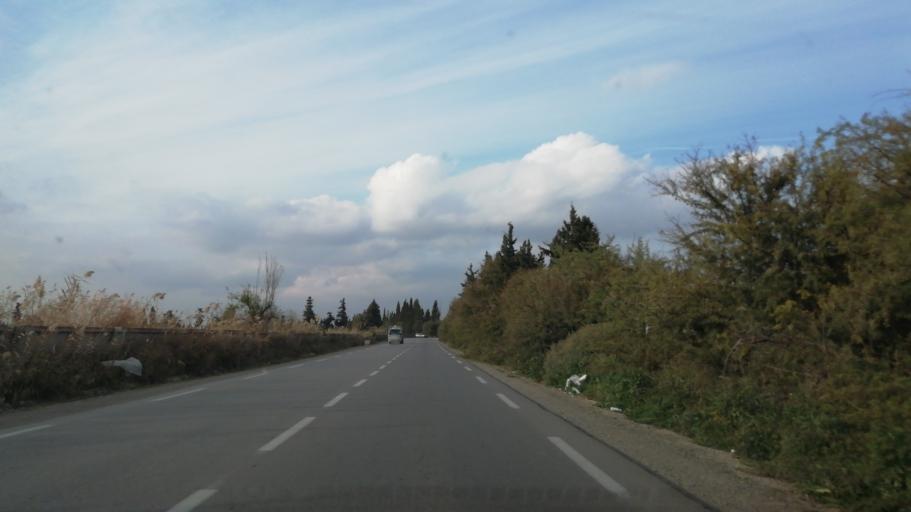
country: DZ
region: Mascara
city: Mascara
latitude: 35.6298
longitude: 0.0409
